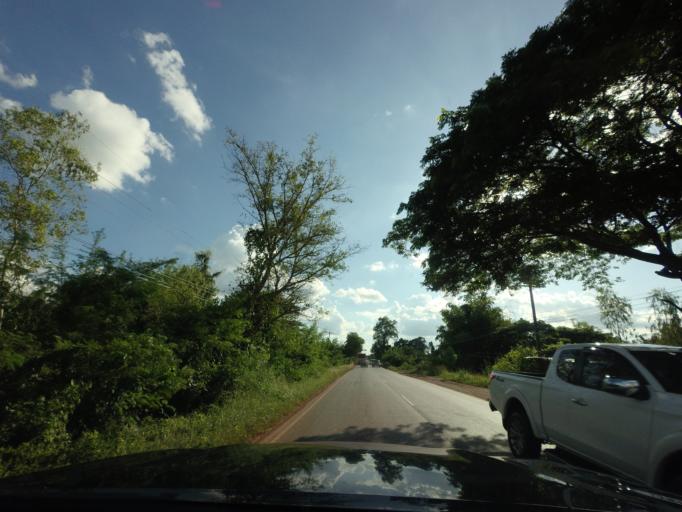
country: TH
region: Changwat Udon Thani
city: Ban Dung
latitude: 17.7430
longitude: 103.2608
